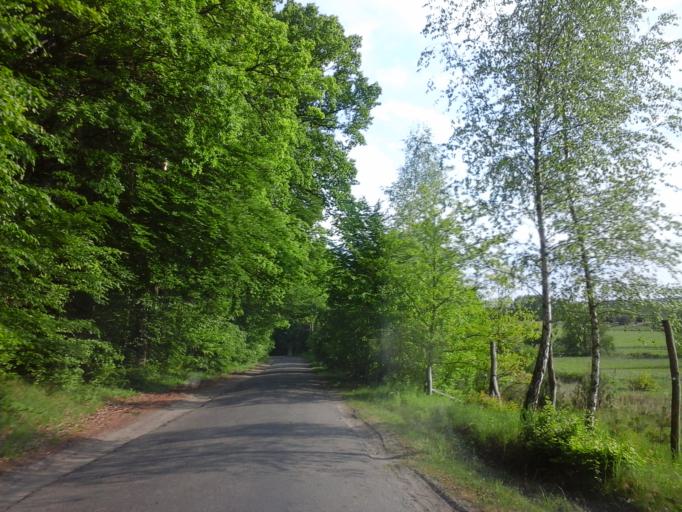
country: PL
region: West Pomeranian Voivodeship
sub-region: Powiat mysliborski
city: Barlinek
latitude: 53.0171
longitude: 15.2217
